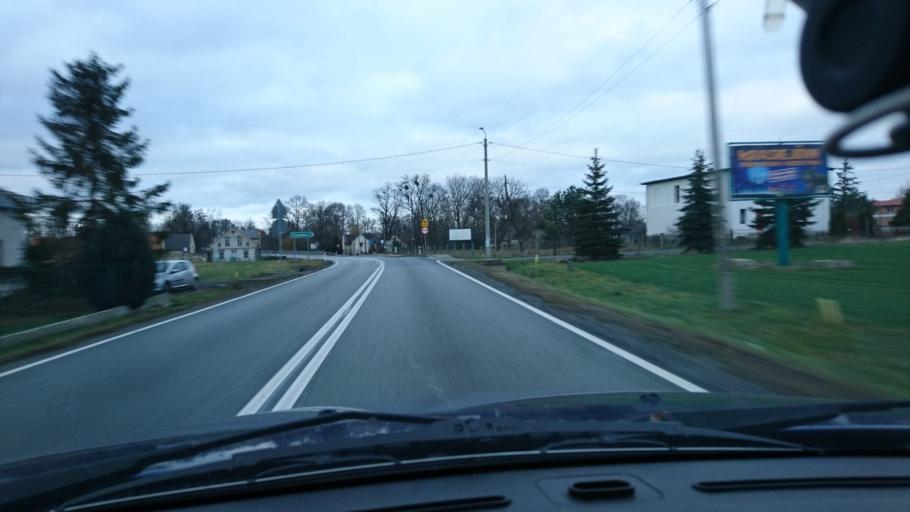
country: PL
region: Opole Voivodeship
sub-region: Powiat kluczborski
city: Byczyna
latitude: 51.0607
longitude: 18.2001
